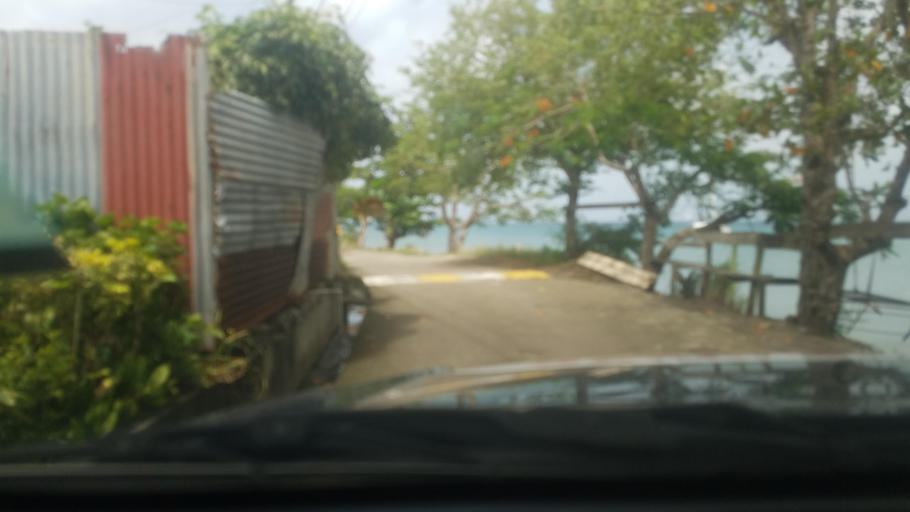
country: LC
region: Laborie Quarter
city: Laborie
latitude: 13.7489
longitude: -60.9952
